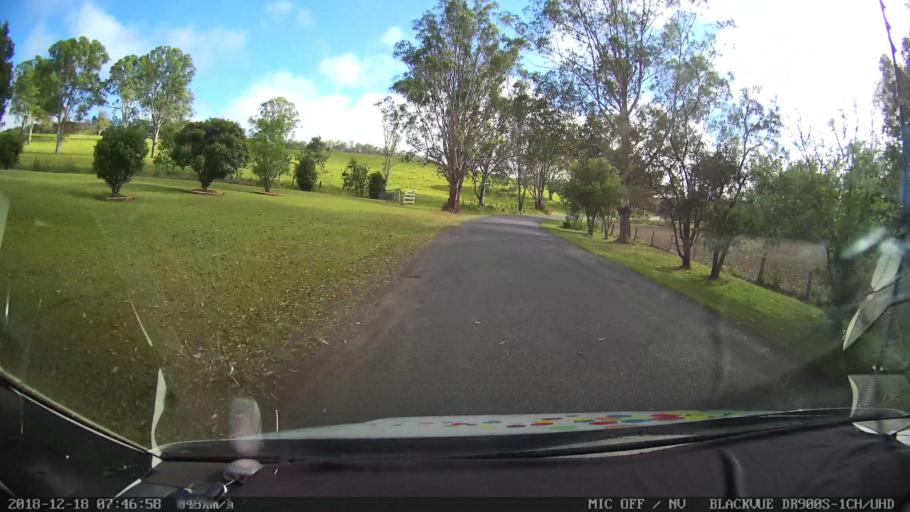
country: AU
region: New South Wales
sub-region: Kyogle
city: Kyogle
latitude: -28.4646
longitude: 152.5537
